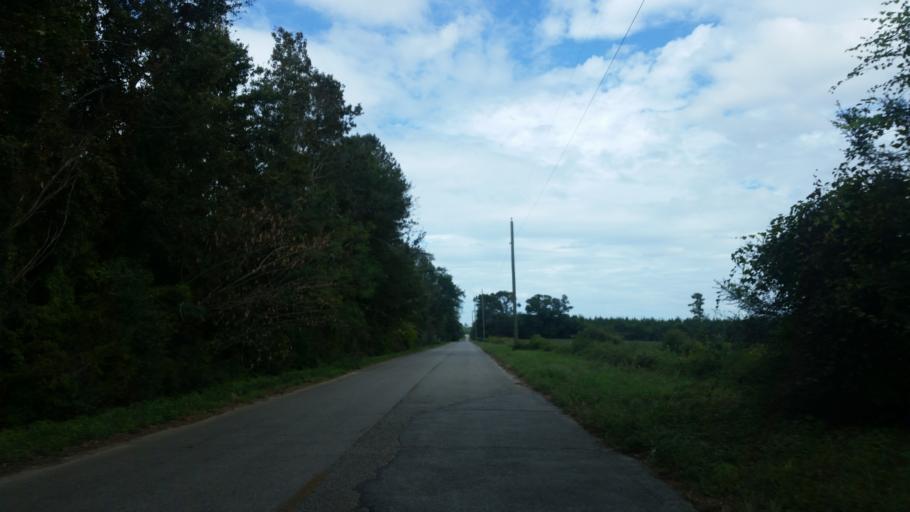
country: US
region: Florida
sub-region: Santa Rosa County
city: Point Baker
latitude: 30.7185
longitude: -86.9928
